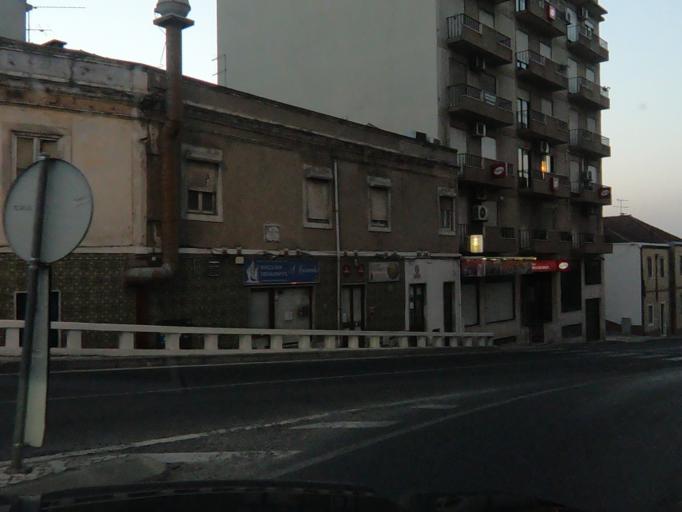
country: PT
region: Santarem
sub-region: Santarem
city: Santarem
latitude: 39.2372
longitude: -8.6893
